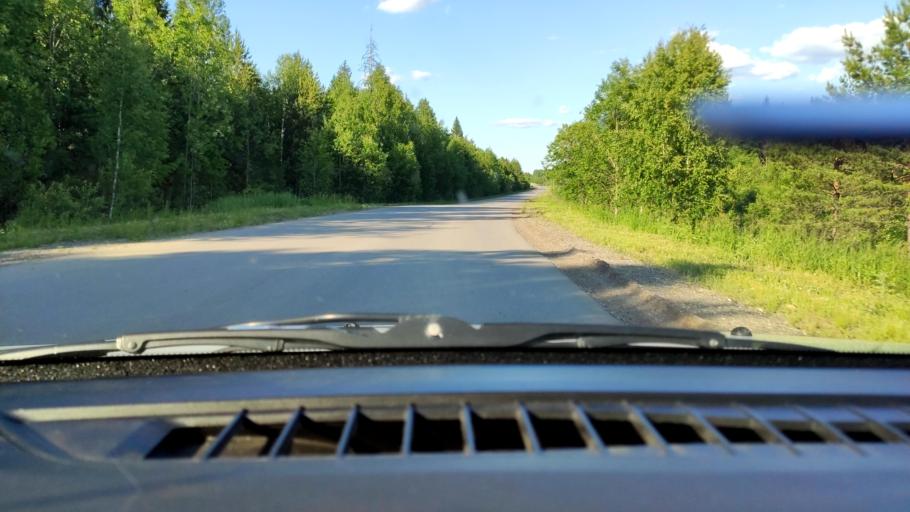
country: RU
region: Perm
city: Orda
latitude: 57.1259
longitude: 56.6852
